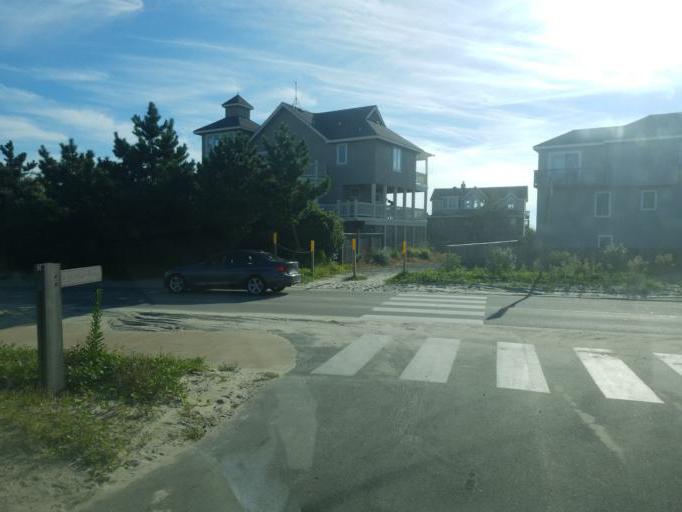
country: US
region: North Carolina
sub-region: Currituck County
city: Currituck
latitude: 36.3940
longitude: -75.8304
